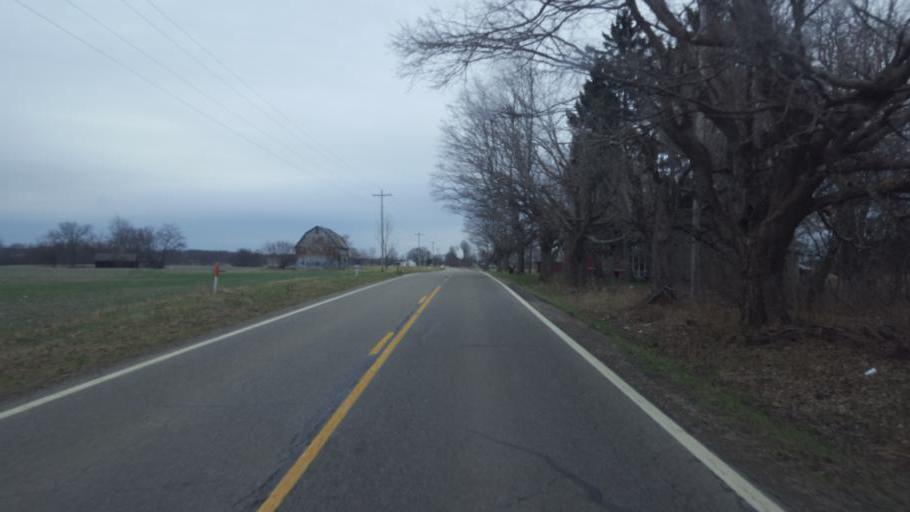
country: US
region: Ohio
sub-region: Knox County
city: Fredericktown
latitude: 40.4775
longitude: -82.6762
